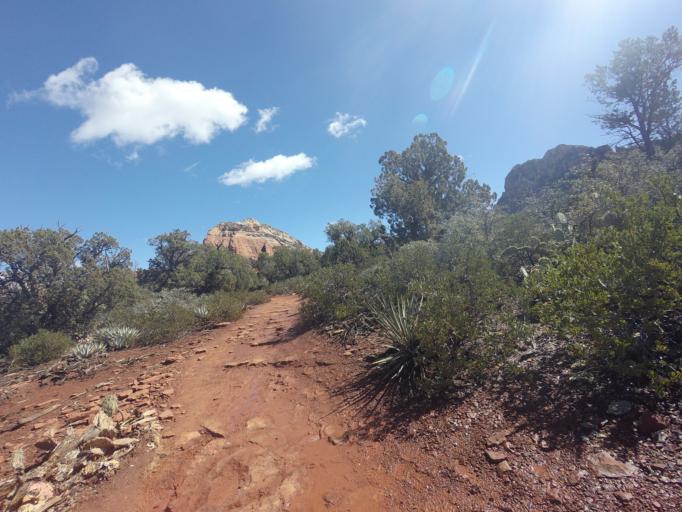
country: US
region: Arizona
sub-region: Yavapai County
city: West Sedona
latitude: 34.9035
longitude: -111.8177
